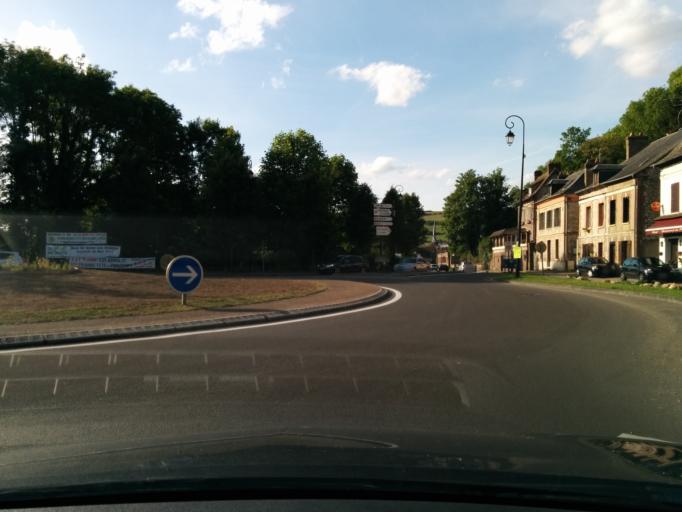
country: FR
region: Haute-Normandie
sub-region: Departement de l'Eure
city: Les Andelys
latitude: 49.2368
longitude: 1.4015
